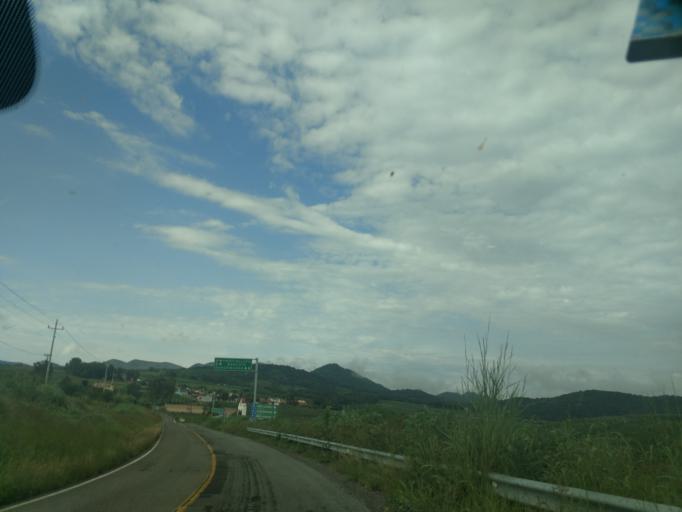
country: MX
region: Jalisco
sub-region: Atengo
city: Soyatlan del Oro
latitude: 20.5271
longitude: -104.3349
